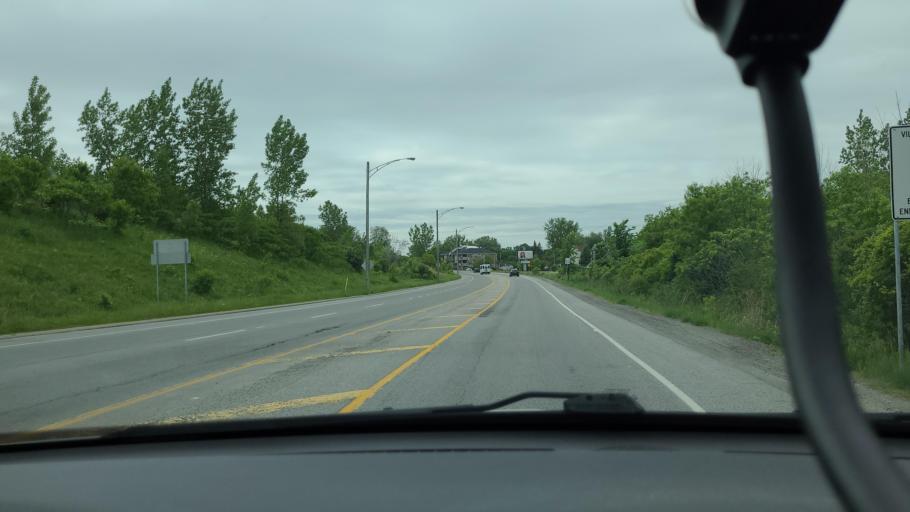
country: CA
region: Quebec
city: Bois-des-Filion
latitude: 45.6554
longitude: -73.7467
